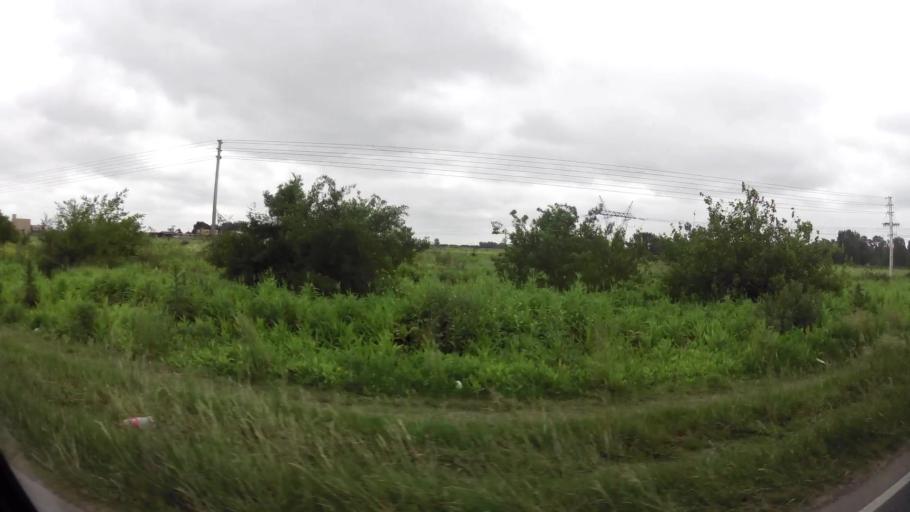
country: AR
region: Buenos Aires
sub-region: Partido de San Vicente
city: San Vicente
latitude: -34.9548
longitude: -58.4636
